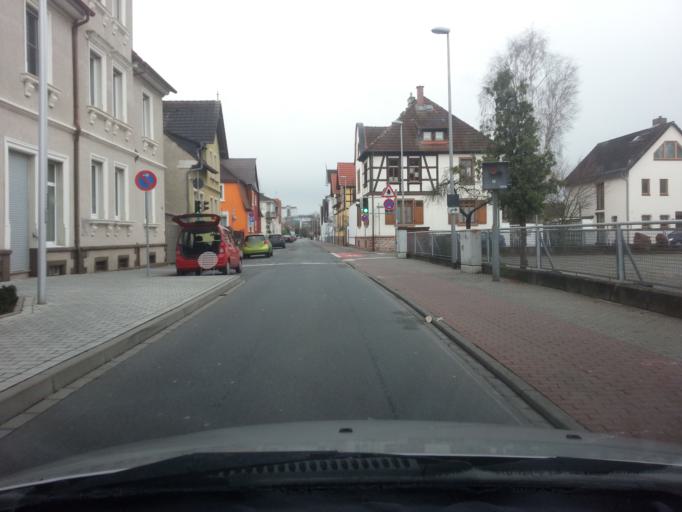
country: DE
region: Hesse
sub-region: Regierungsbezirk Darmstadt
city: Gross-Gerau
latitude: 49.9187
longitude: 8.4815
